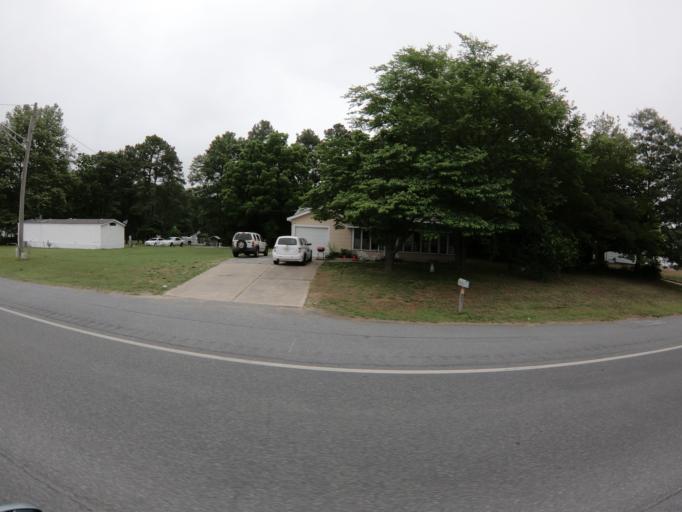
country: US
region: Delaware
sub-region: Sussex County
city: Milton
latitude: 38.8207
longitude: -75.3054
